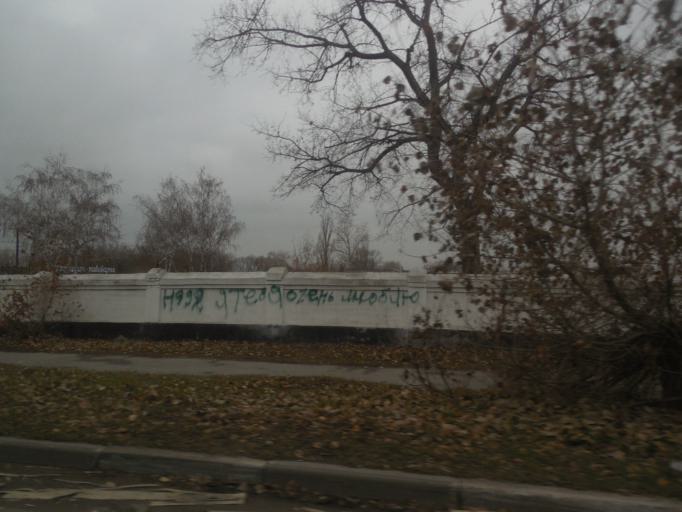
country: RU
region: Lipetsk
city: Zadonsk
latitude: 52.3937
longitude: 38.9165
